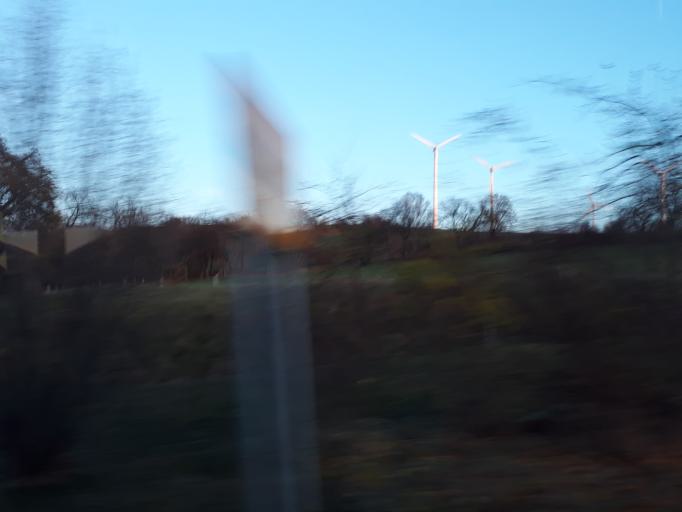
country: DE
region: Saxony
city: Reinhardtsgrimma
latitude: 50.9041
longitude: 13.7867
